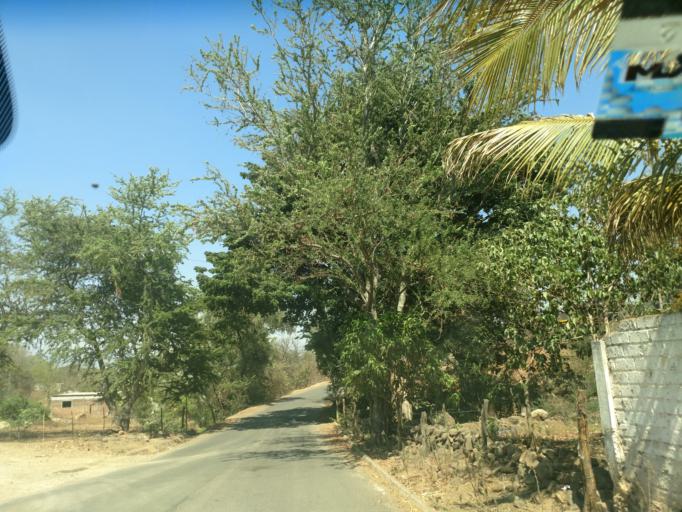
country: MX
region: Nayarit
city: Santa Maria del Oro
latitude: 21.4694
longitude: -104.6596
